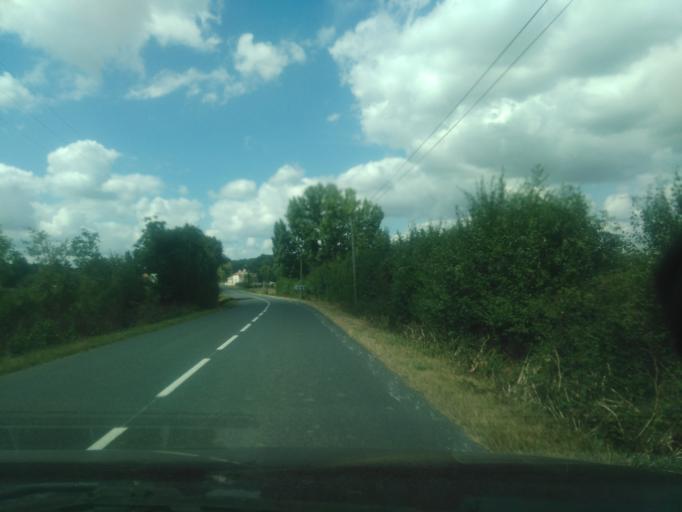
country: FR
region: Pays de la Loire
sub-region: Departement de la Vendee
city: Chauche
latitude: 46.8491
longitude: -1.2962
